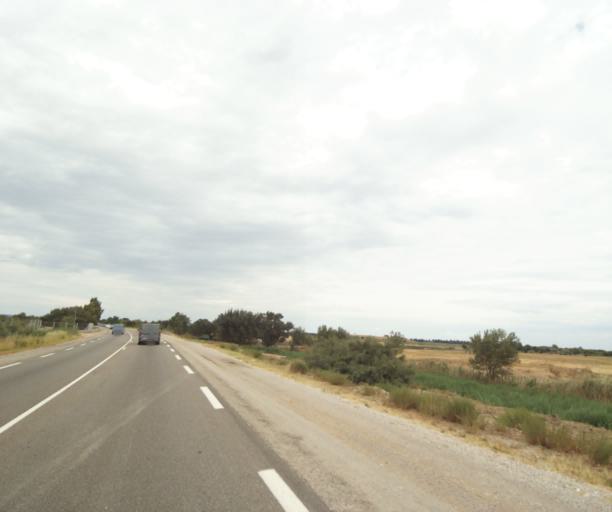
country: FR
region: Languedoc-Roussillon
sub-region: Departement de l'Herault
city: Saint-Just
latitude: 43.6267
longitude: 4.1279
